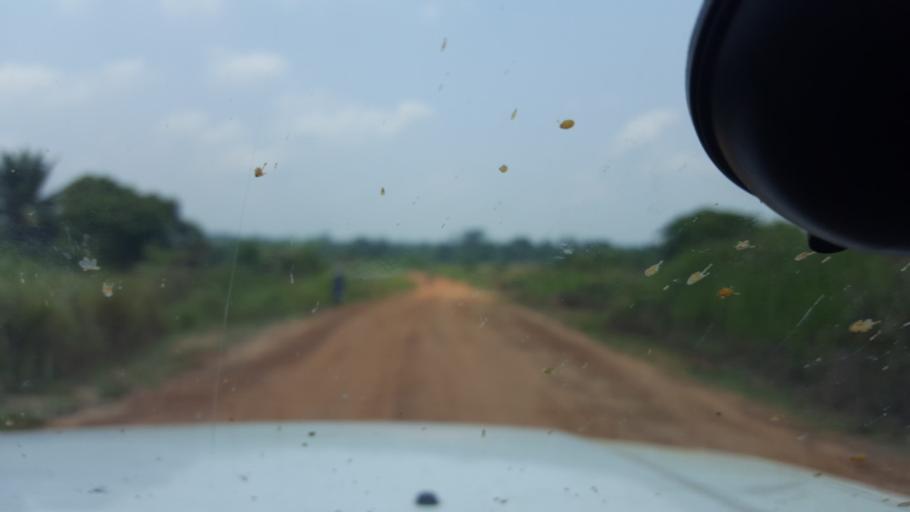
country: CD
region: Bandundu
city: Mushie
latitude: -3.7443
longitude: 16.6554
